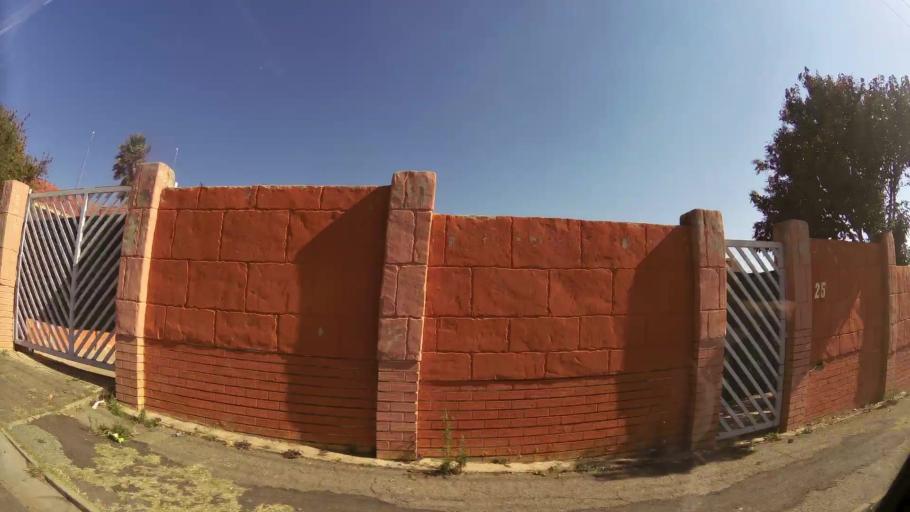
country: ZA
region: Gauteng
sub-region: City of Johannesburg Metropolitan Municipality
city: Johannesburg
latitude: -26.2472
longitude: 28.0852
